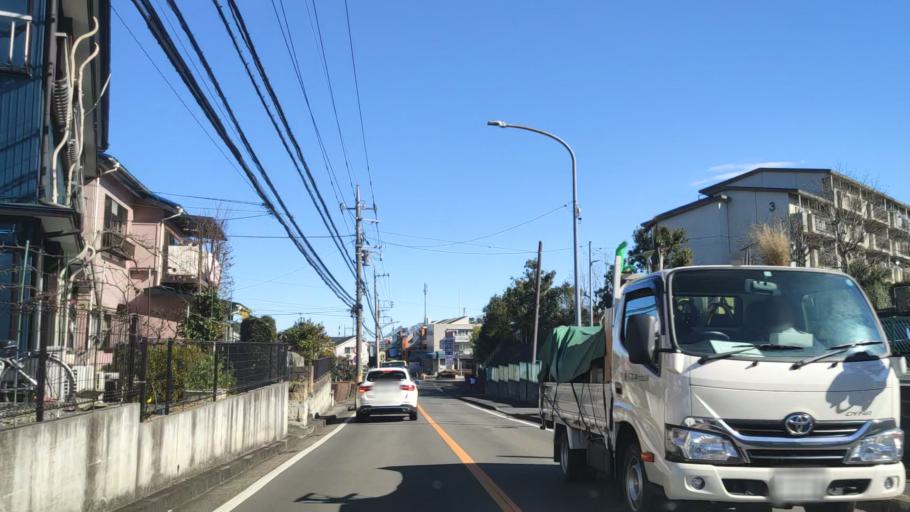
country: JP
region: Tokyo
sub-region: Machida-shi
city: Machida
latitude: 35.5108
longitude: 139.5239
